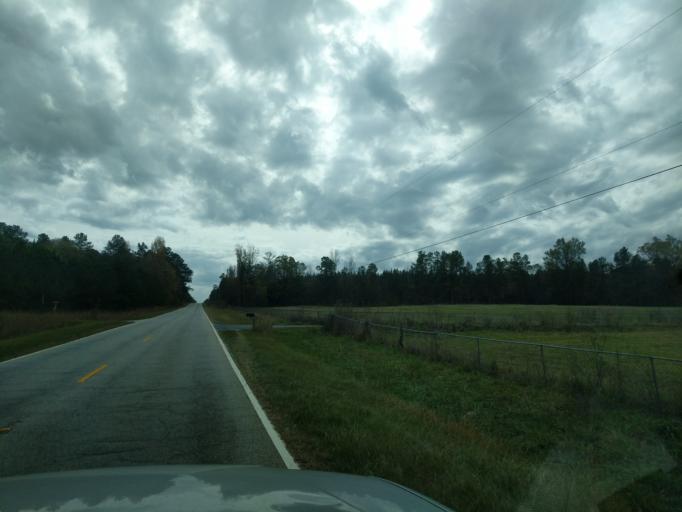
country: US
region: South Carolina
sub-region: Saluda County
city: Saluda
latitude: 34.1485
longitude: -81.8474
